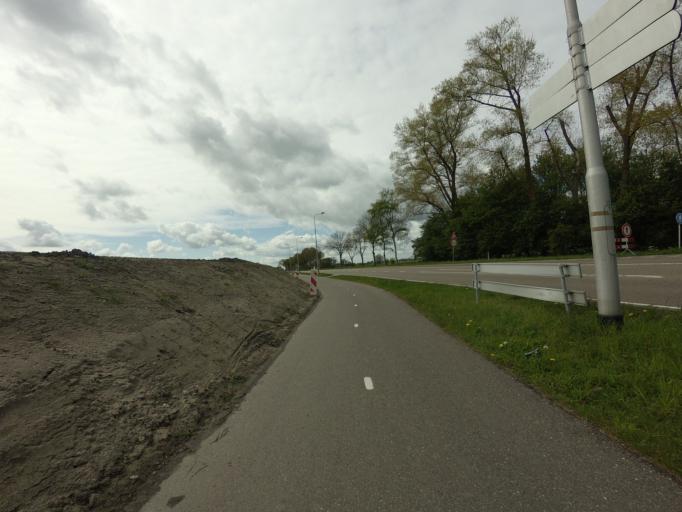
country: NL
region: North Holland
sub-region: Gemeente Weesp
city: Weesp
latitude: 52.2912
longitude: 5.0836
